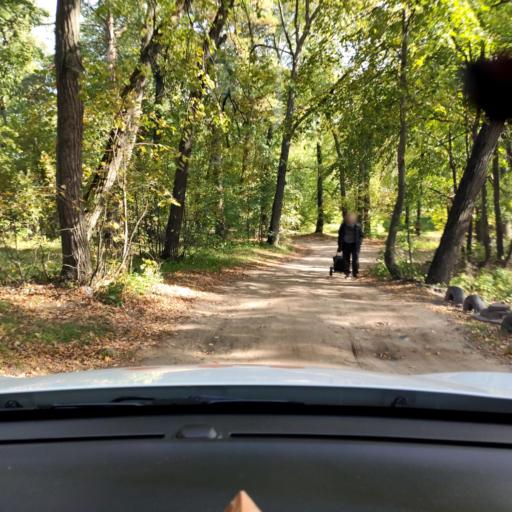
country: RU
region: Tatarstan
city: Staroye Arakchino
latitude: 55.8071
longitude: 49.0141
